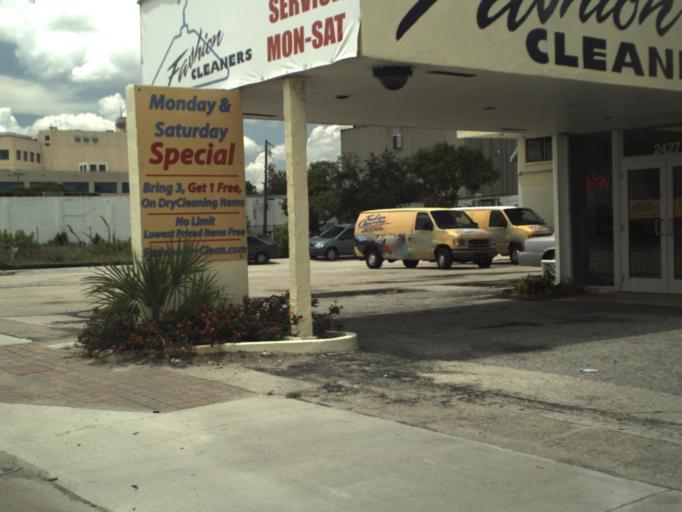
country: US
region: Florida
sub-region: Broward County
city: Boulevard Gardens
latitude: 26.1218
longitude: -80.1746
